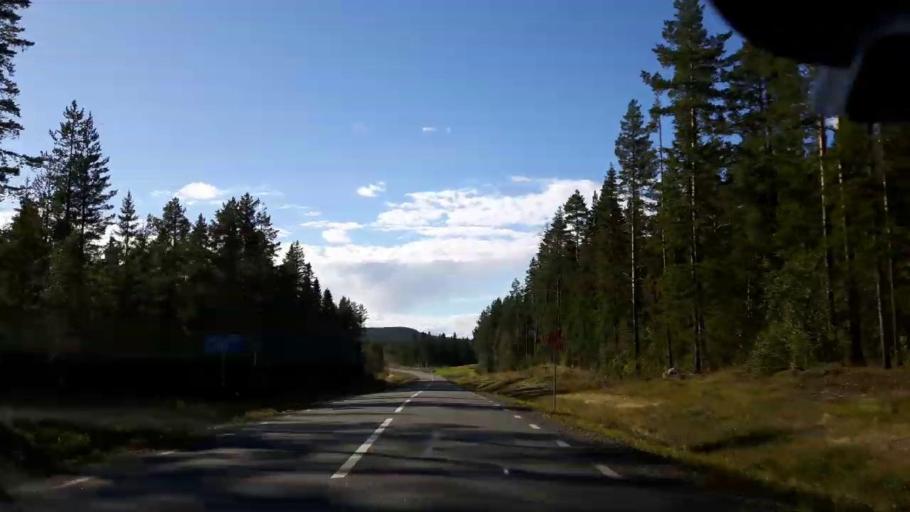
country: SE
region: Jaemtland
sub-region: Stroemsunds Kommun
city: Stroemsund
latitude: 63.5388
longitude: 15.9930
